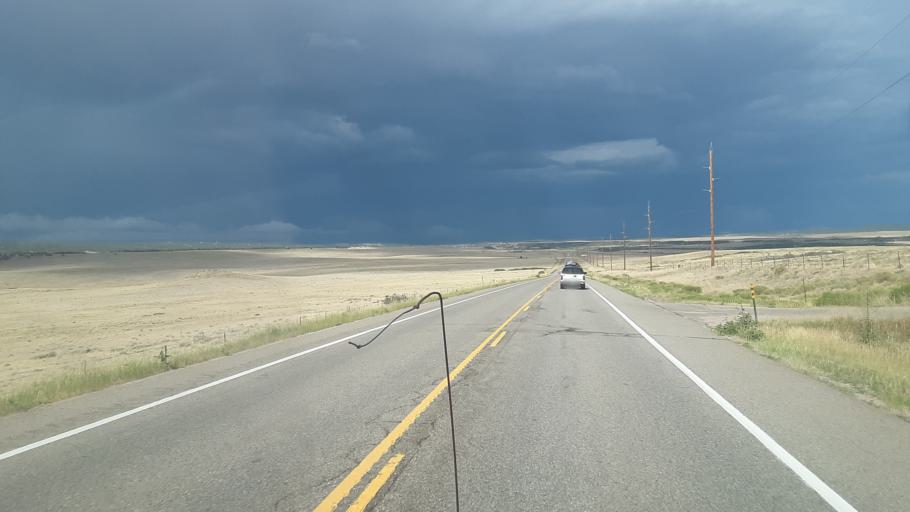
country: US
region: Colorado
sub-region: Huerfano County
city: Walsenburg
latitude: 37.5492
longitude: -104.9850
